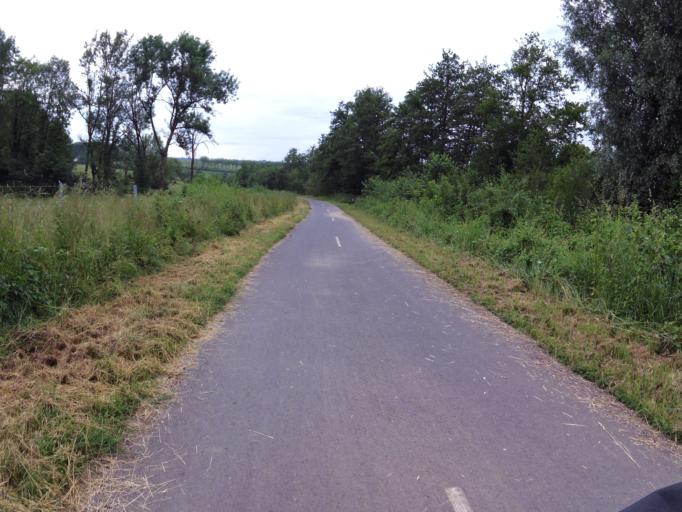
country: FR
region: Champagne-Ardenne
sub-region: Departement des Ardennes
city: Donchery
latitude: 49.6986
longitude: 4.8995
